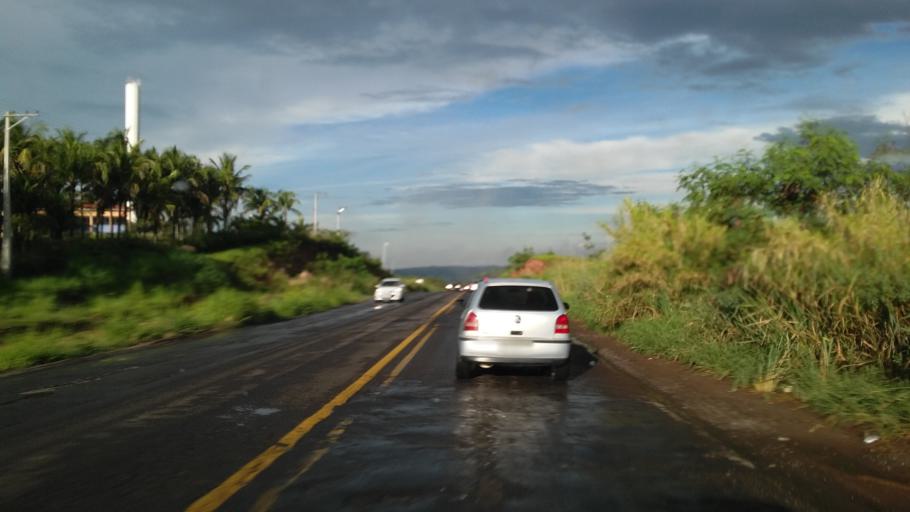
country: BR
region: Sao Paulo
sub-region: Marilia
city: Marilia
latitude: -22.1284
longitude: -49.9380
